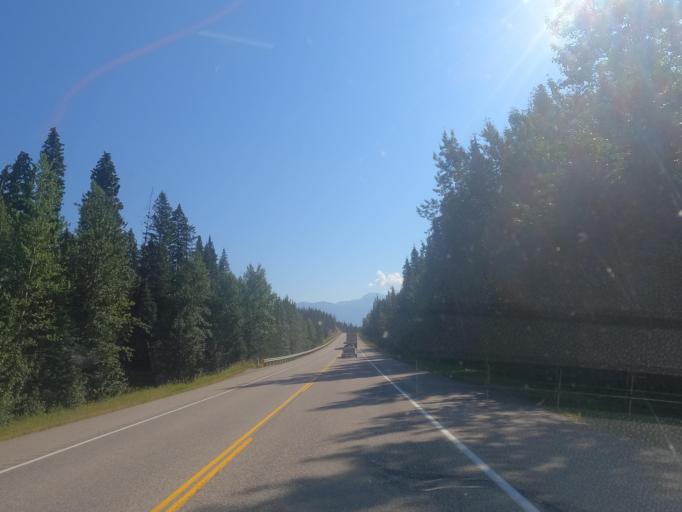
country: CA
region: Alberta
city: Jasper Park Lodge
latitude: 52.8608
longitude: -118.1884
